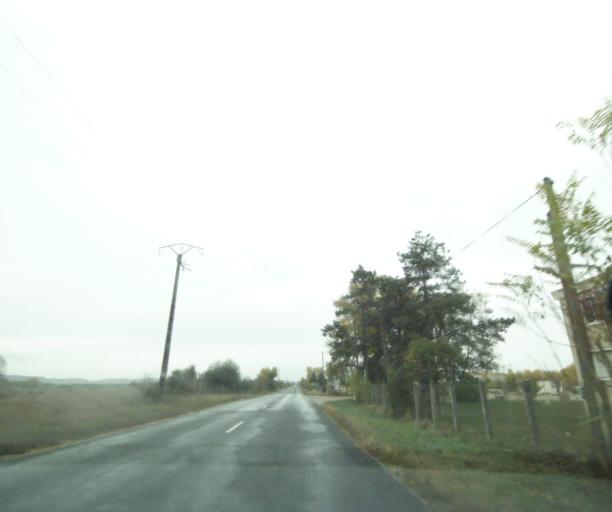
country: FR
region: Rhone-Alpes
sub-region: Departement de l'Ain
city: Saint-Maurice-de-Gourdans
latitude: 45.8093
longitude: 5.2142
